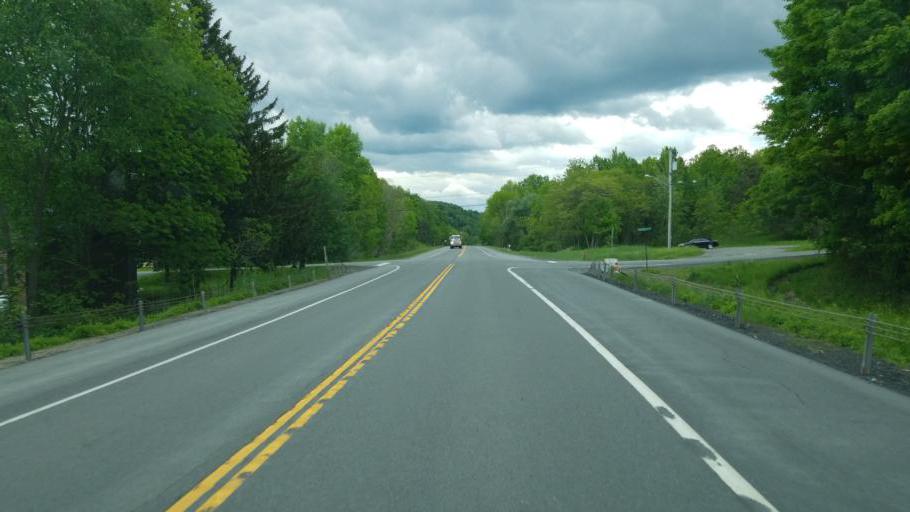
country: US
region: New York
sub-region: Oneida County
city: Chadwicks
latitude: 42.9669
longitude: -75.2510
